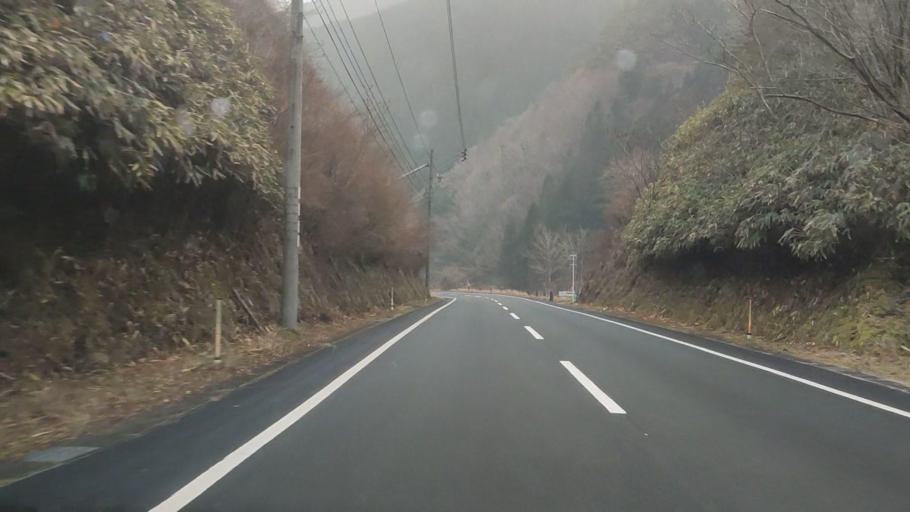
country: JP
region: Kumamoto
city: Matsubase
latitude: 32.5520
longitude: 130.9341
